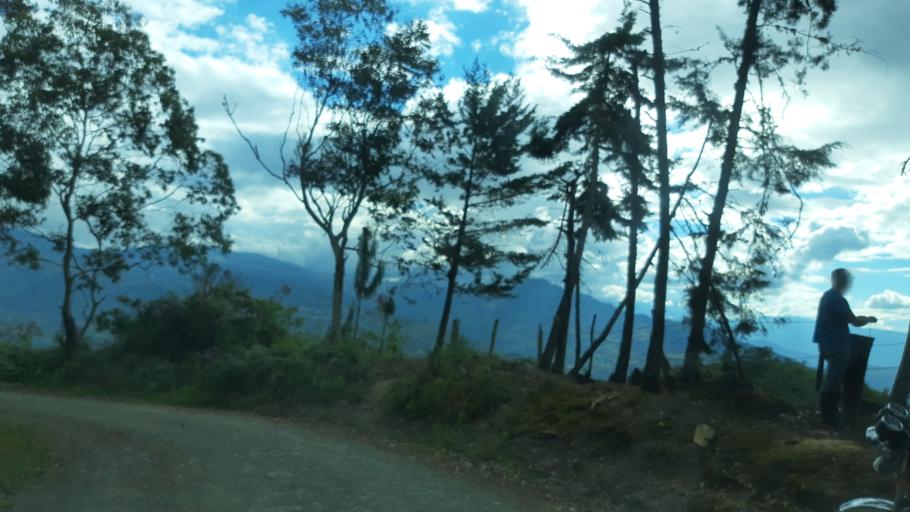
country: CO
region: Boyaca
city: Garagoa
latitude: 5.0082
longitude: -73.3422
